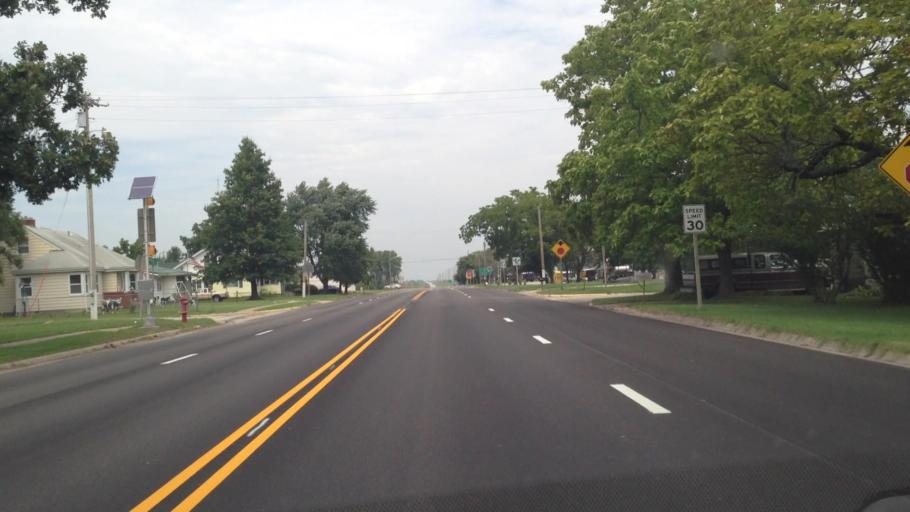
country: US
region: Kansas
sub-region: Allen County
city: Iola
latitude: 37.9193
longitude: -95.1700
